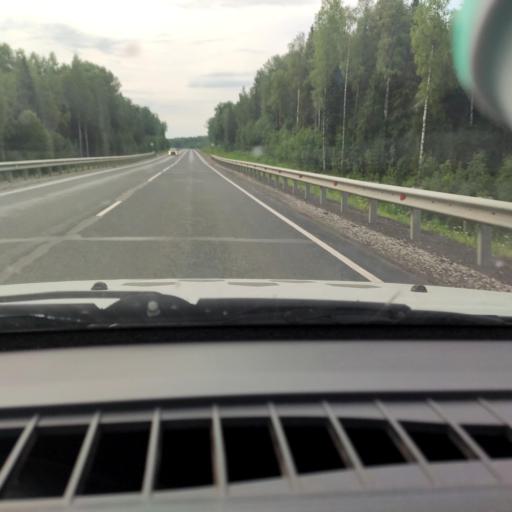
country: RU
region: Kirov
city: Kostino
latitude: 58.6616
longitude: 53.7650
